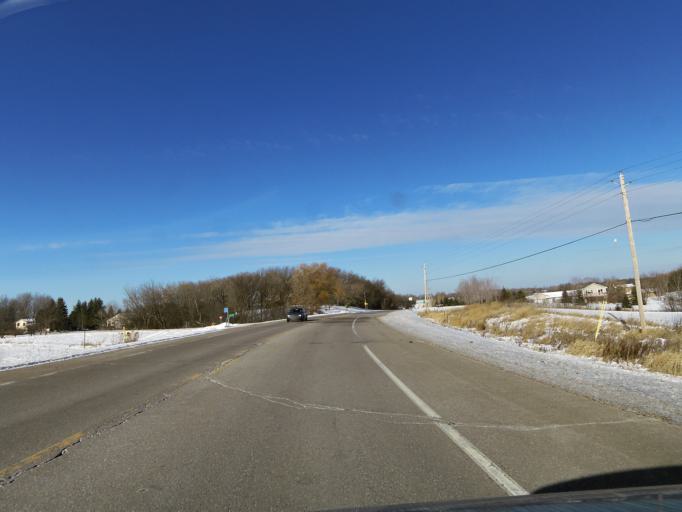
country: US
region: Minnesota
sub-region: Scott County
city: Shakopee
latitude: 44.7347
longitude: -93.4991
